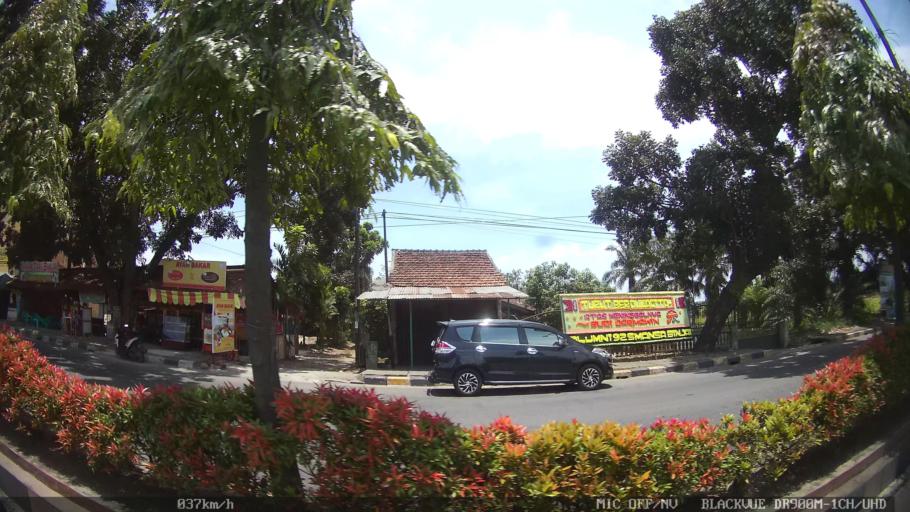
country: ID
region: North Sumatra
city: Binjai
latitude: 3.6063
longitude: 98.5283
